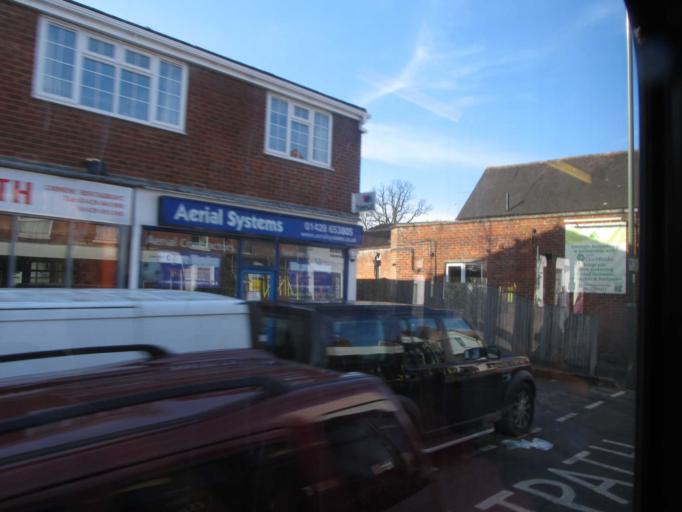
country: GB
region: England
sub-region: Surrey
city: Haslemere
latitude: 51.0879
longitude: -0.7291
